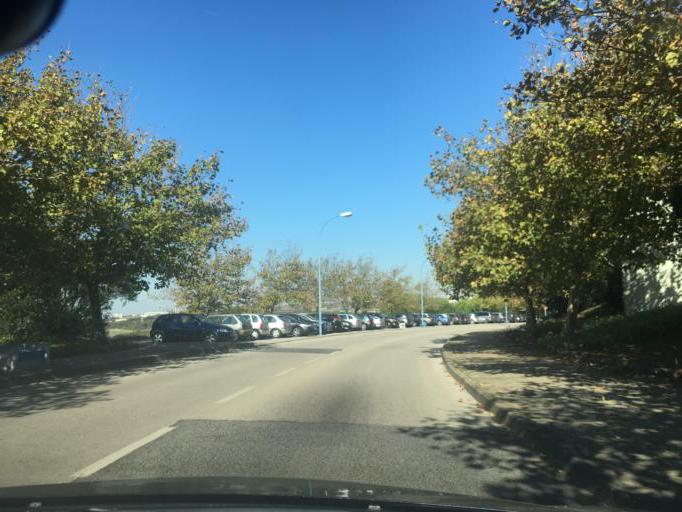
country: PT
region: Lisbon
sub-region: Oeiras
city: Porto Salvo
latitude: 38.7401
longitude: -9.3060
